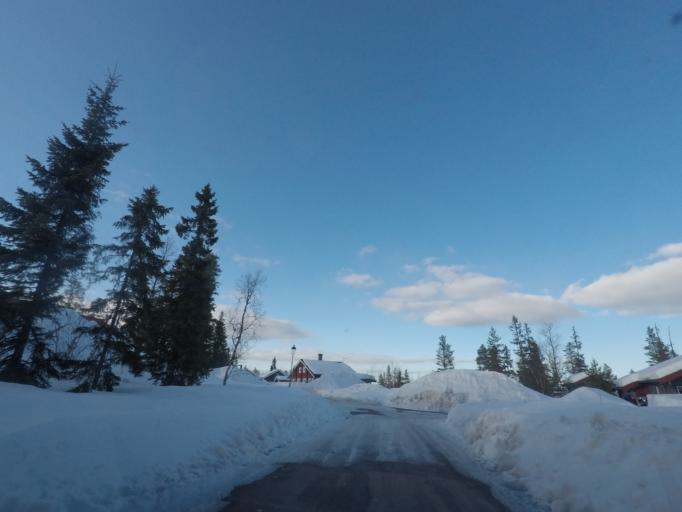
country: SE
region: Dalarna
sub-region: Malung-Saelens kommun
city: Malung
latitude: 61.1717
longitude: 13.1894
